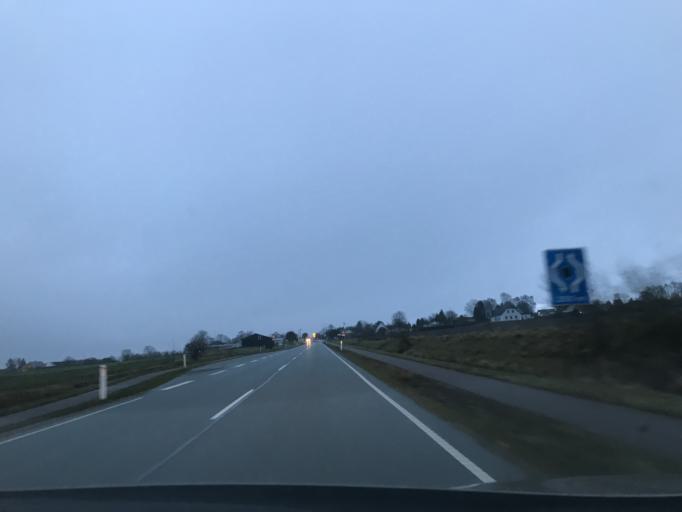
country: DK
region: Central Jutland
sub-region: Hedensted Kommune
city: Hornsyld
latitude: 55.7046
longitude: 9.7799
